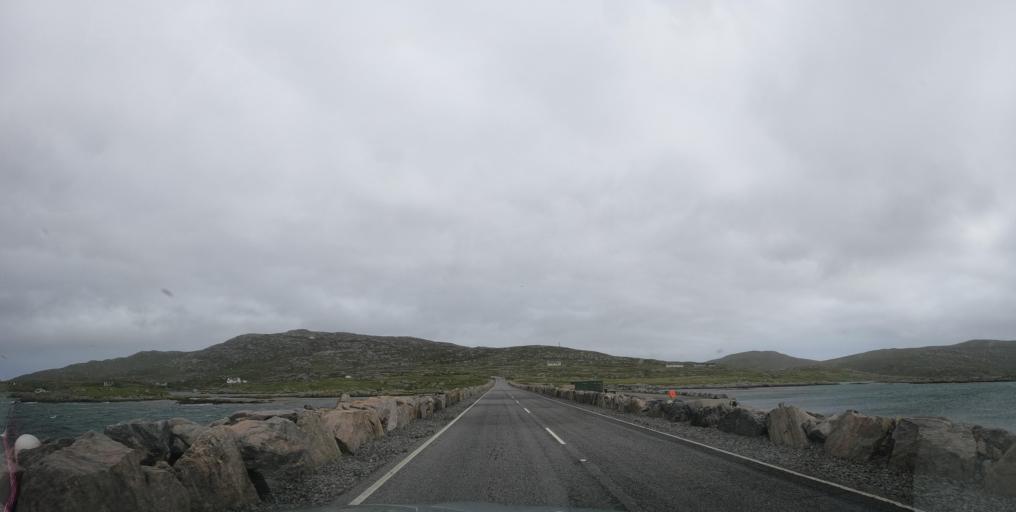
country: GB
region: Scotland
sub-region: Eilean Siar
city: Isle of South Uist
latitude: 57.1010
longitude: -7.3177
